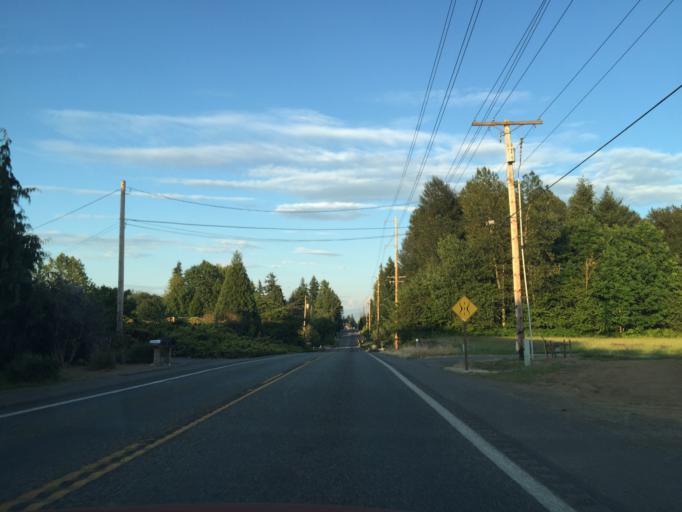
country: US
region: Washington
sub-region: Whatcom County
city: Lynden
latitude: 48.9353
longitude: -122.5399
